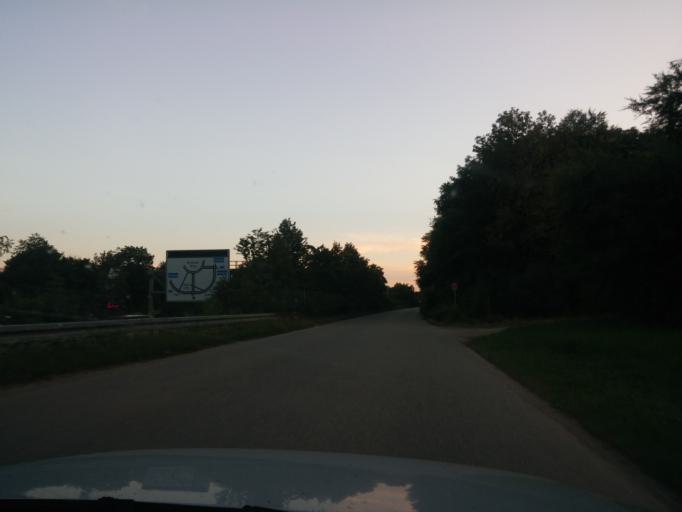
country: DE
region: Bavaria
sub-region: Upper Bavaria
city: Kirchheim bei Muenchen
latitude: 48.1464
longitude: 11.7794
